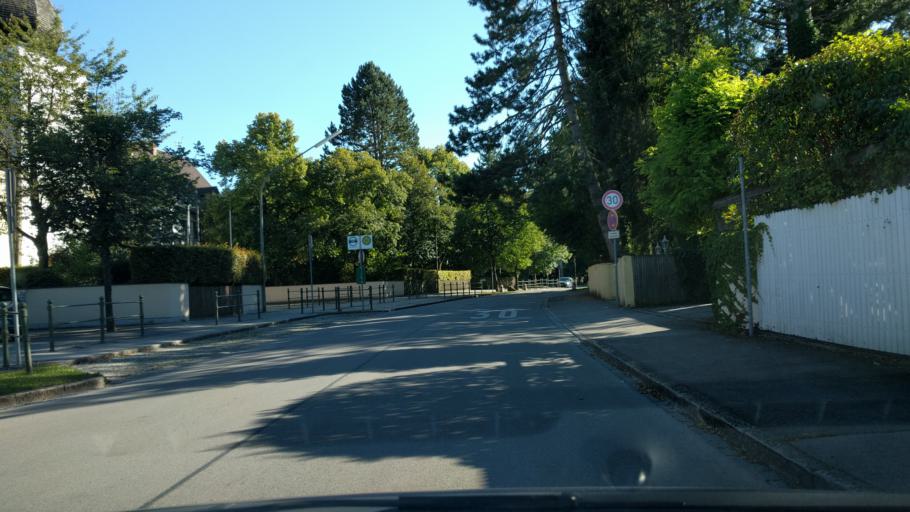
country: DE
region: Bavaria
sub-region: Upper Bavaria
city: Grunwald
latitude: 48.0449
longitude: 11.5239
